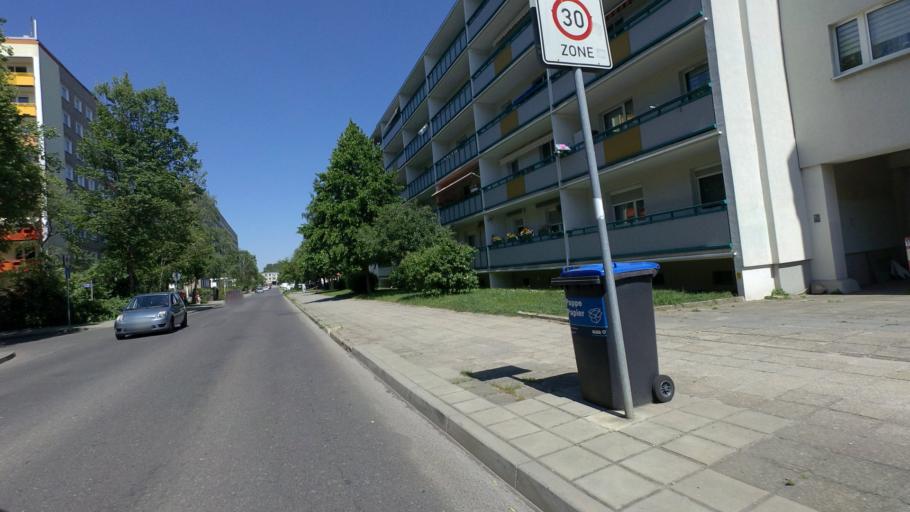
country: DE
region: Brandenburg
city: Cottbus
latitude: 51.7626
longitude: 14.3433
